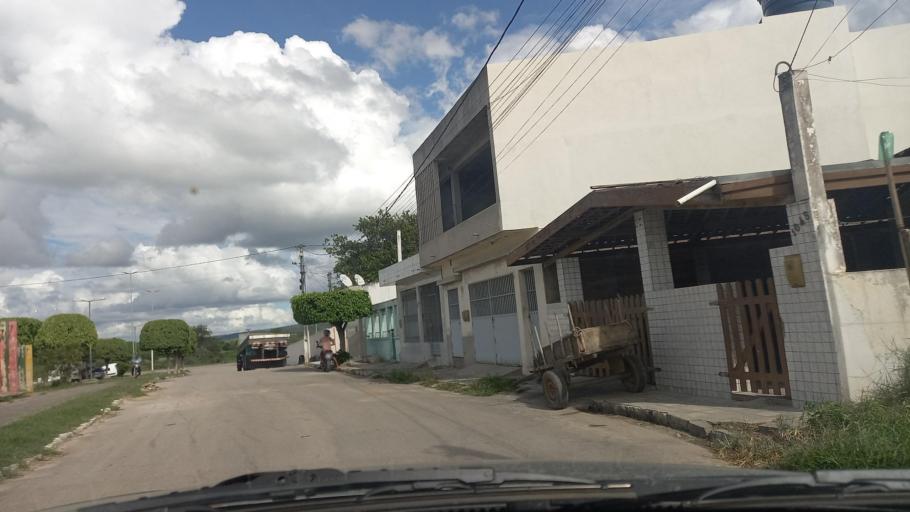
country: BR
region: Pernambuco
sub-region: Cachoeirinha
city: Cachoeirinha
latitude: -8.4931
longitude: -36.2384
